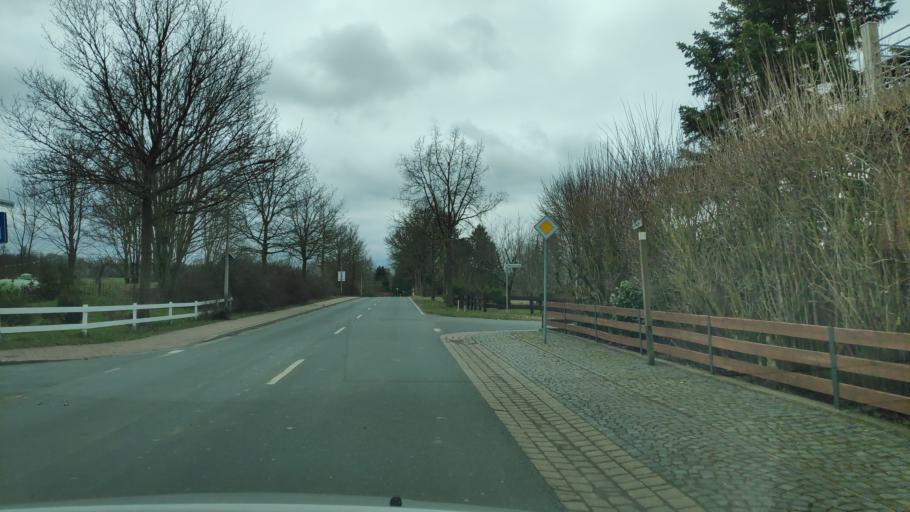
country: DE
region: Lower Saxony
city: Hessisch Oldendorf
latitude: 52.2122
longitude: 9.2936
